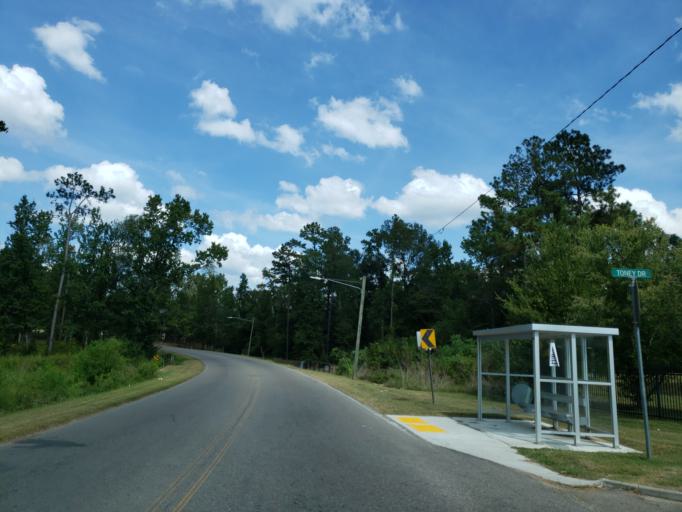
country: US
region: Mississippi
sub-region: Forrest County
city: Hattiesburg
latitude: 31.3001
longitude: -89.2948
